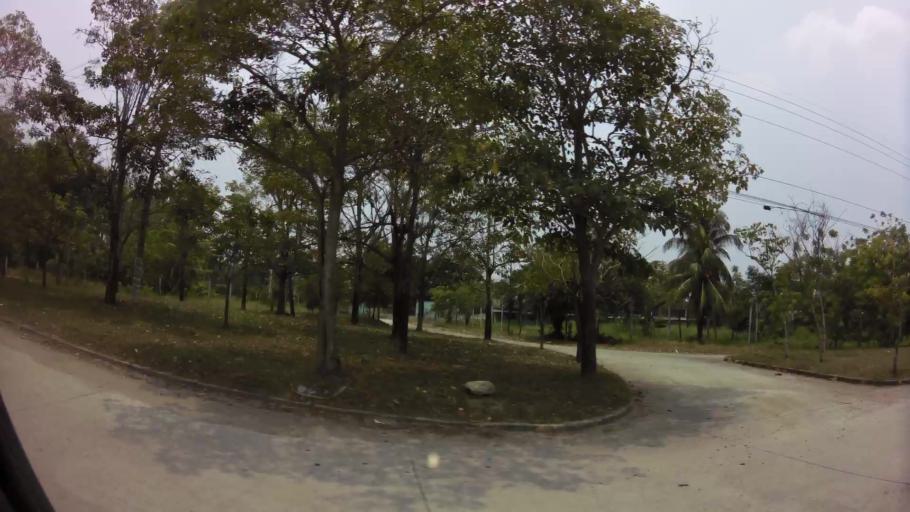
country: HN
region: Yoro
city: El Progreso
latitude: 15.4076
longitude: -87.8319
